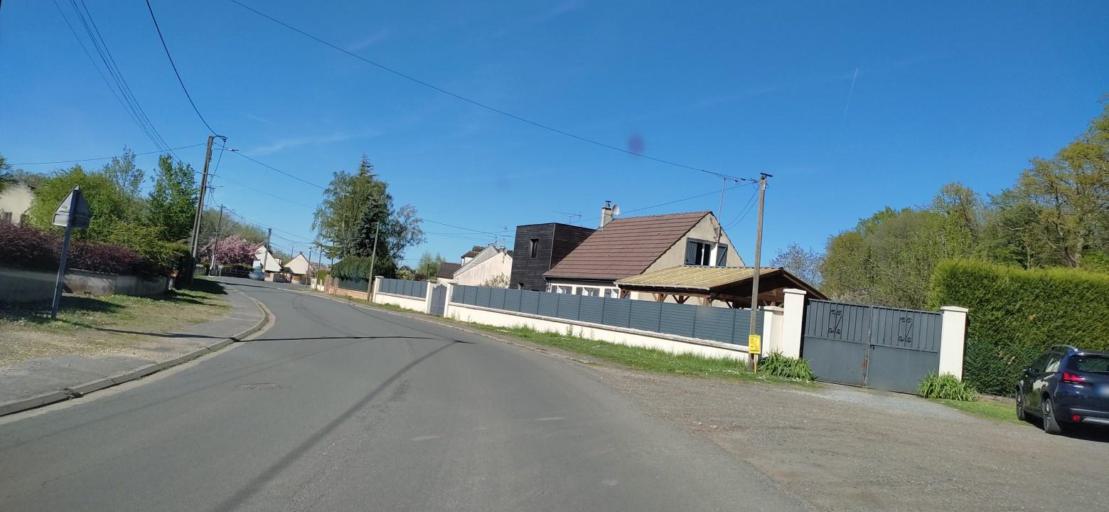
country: FR
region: Picardie
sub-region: Departement de l'Oise
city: Tracy-le-Mont
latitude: 49.4854
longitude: 2.9583
